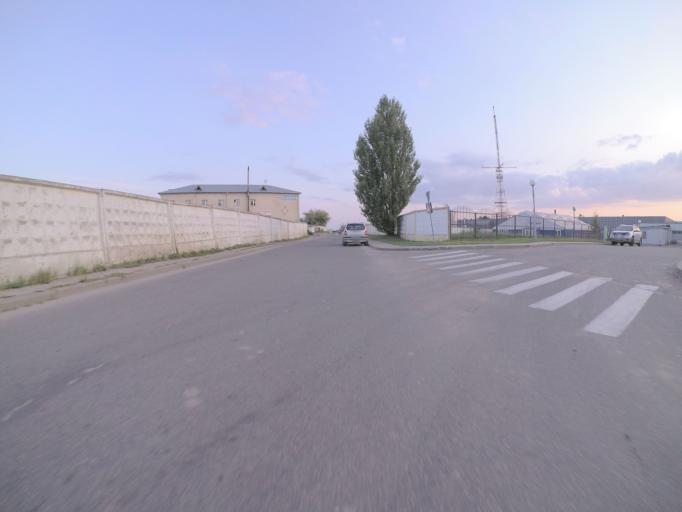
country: BY
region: Grodnenskaya
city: Hrodna
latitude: 53.7057
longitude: 23.8283
